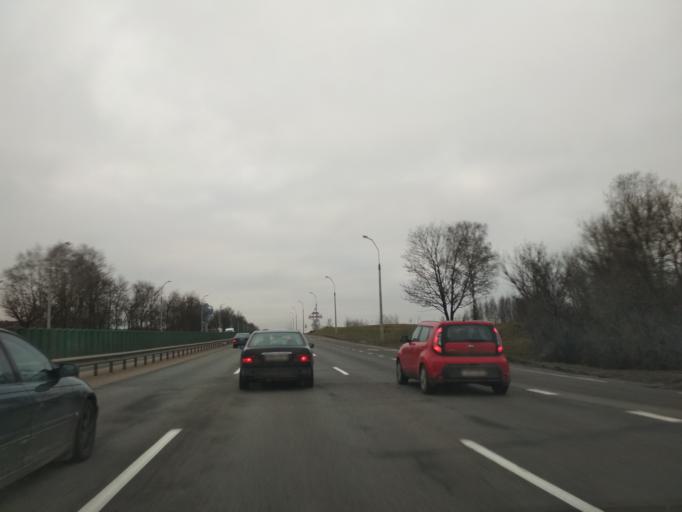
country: BY
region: Minsk
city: Vyaliki Trastsyanets
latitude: 53.8436
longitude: 27.7148
